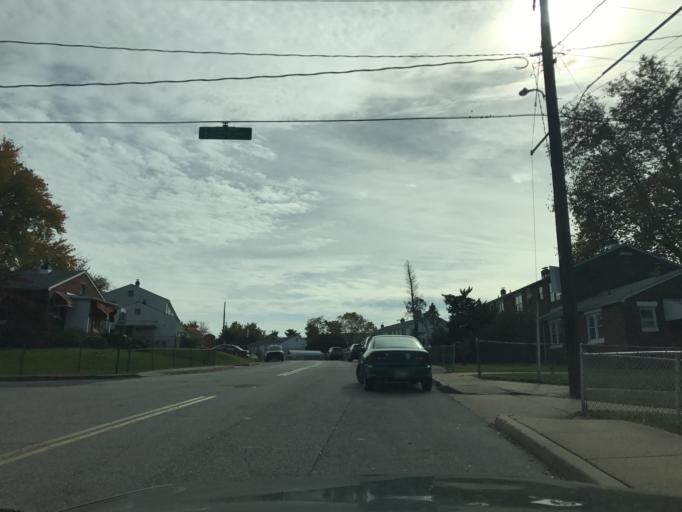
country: US
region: Maryland
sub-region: Baltimore County
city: Rosedale
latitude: 39.3070
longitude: -76.5564
